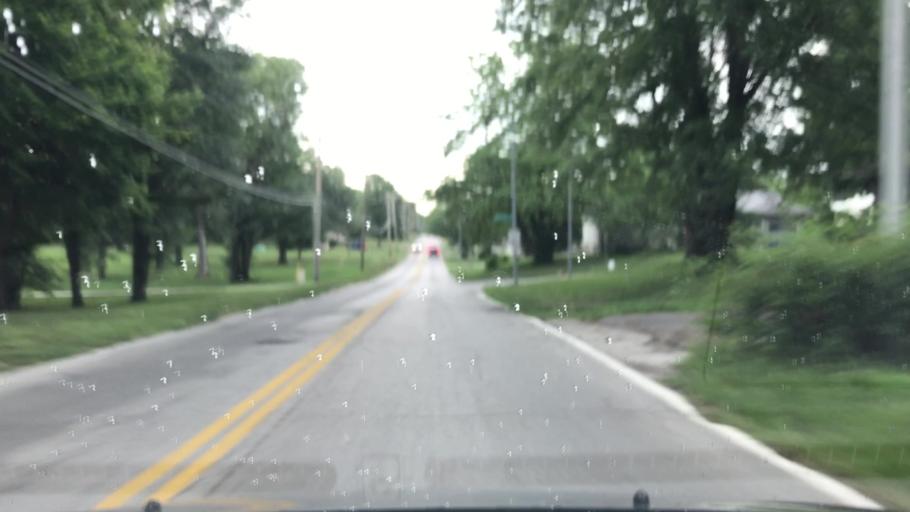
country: US
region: Missouri
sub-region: Jackson County
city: Grandview
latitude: 38.9301
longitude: -94.4971
